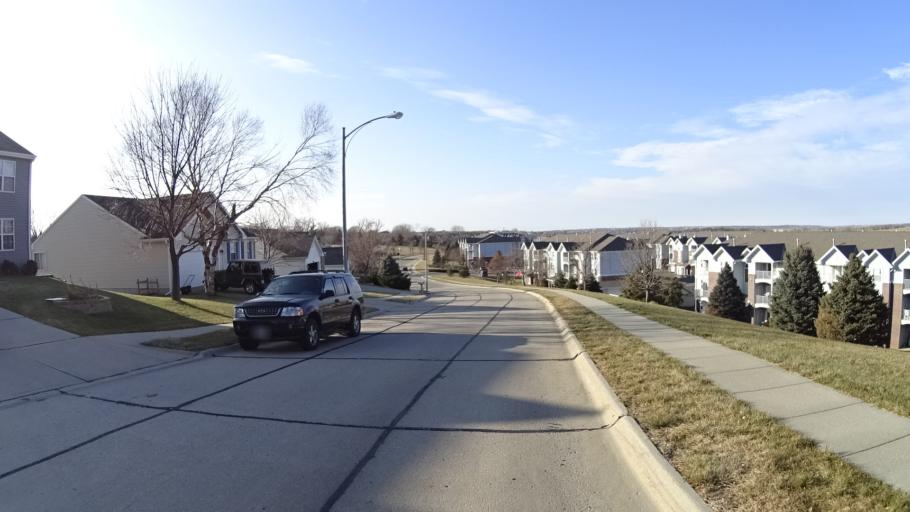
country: US
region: Nebraska
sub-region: Sarpy County
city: Offutt Air Force Base
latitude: 41.1354
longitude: -95.9524
